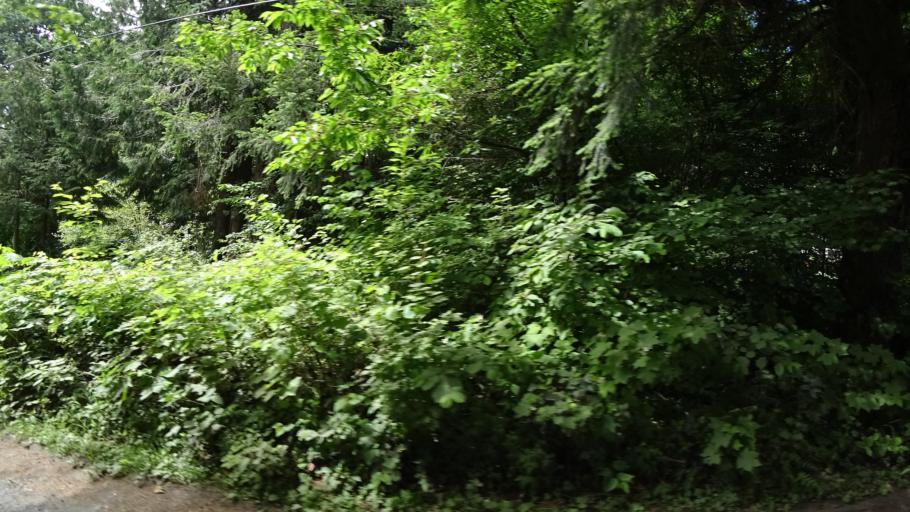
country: US
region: Oregon
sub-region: Washington County
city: Bethany
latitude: 45.5976
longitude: -122.8290
